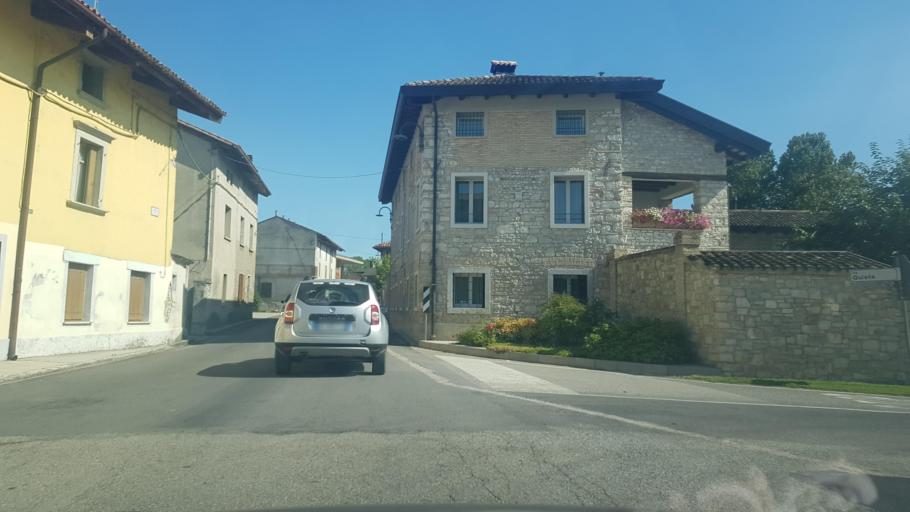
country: IT
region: Friuli Venezia Giulia
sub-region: Provincia di Udine
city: Porpetto
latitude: 45.8707
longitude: 13.2220
